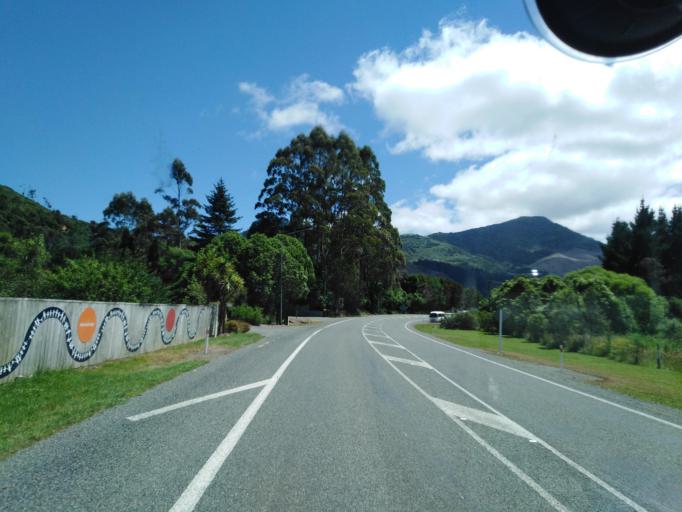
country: NZ
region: Nelson
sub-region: Nelson City
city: Nelson
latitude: -41.2166
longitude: 173.3954
